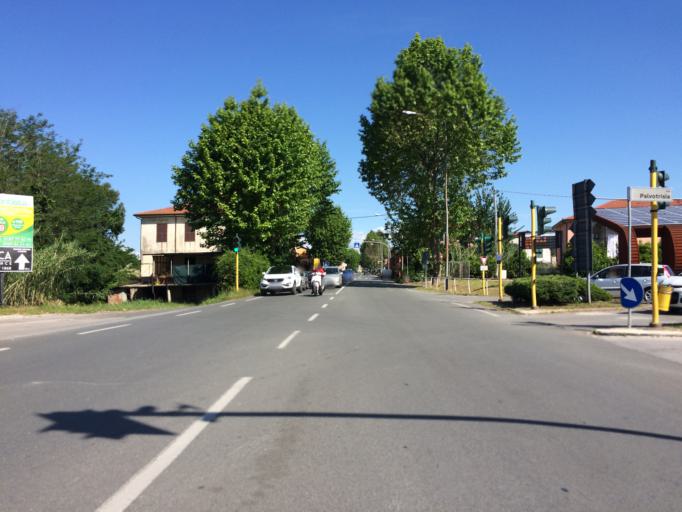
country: IT
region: Liguria
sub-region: Provincia di La Spezia
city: Colombiera-Molicciara
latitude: 44.0771
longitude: 10.0128
